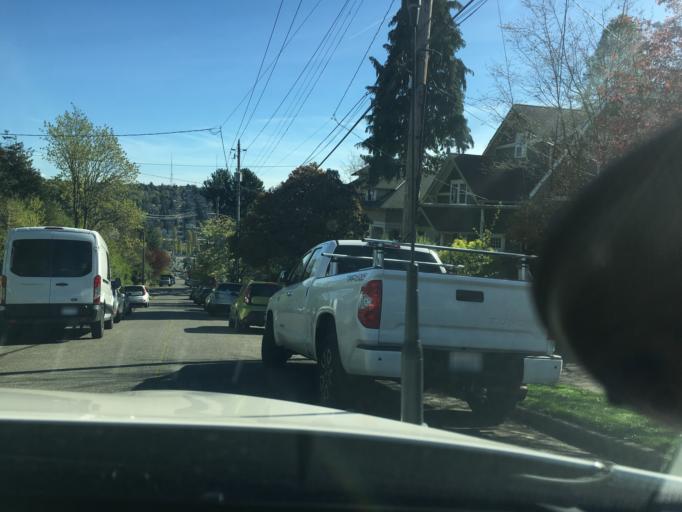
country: US
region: Washington
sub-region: King County
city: Seattle
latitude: 47.6577
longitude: -122.3545
